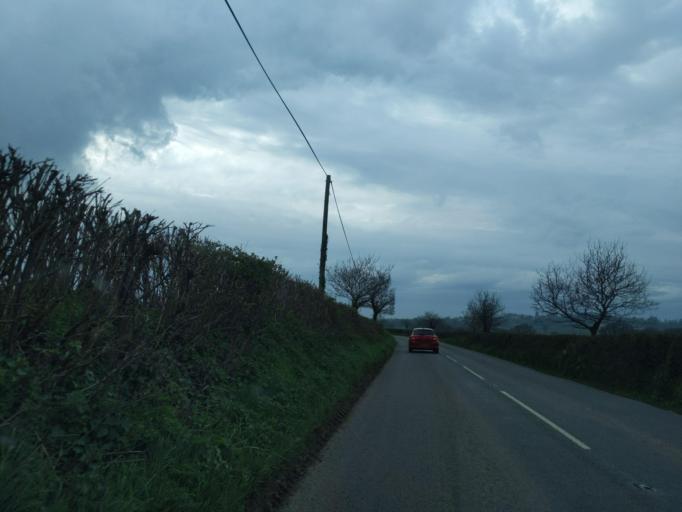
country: GB
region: England
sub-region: Devon
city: Winkleigh
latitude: 50.8488
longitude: -3.9200
